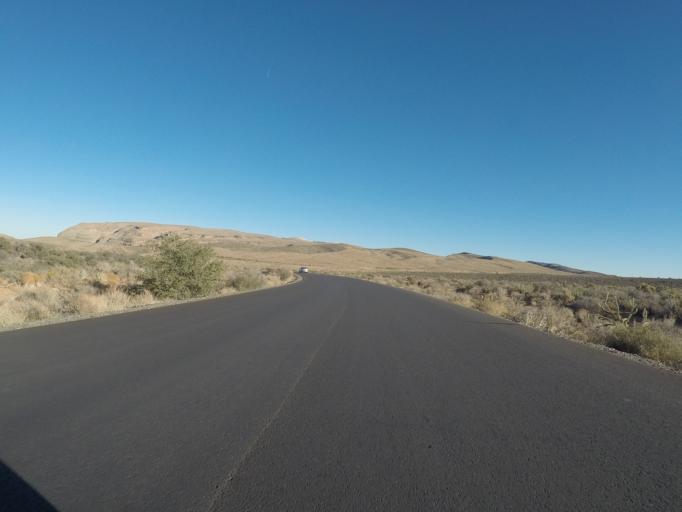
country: US
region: Nevada
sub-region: Clark County
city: Summerlin South
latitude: 36.1165
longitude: -115.4560
